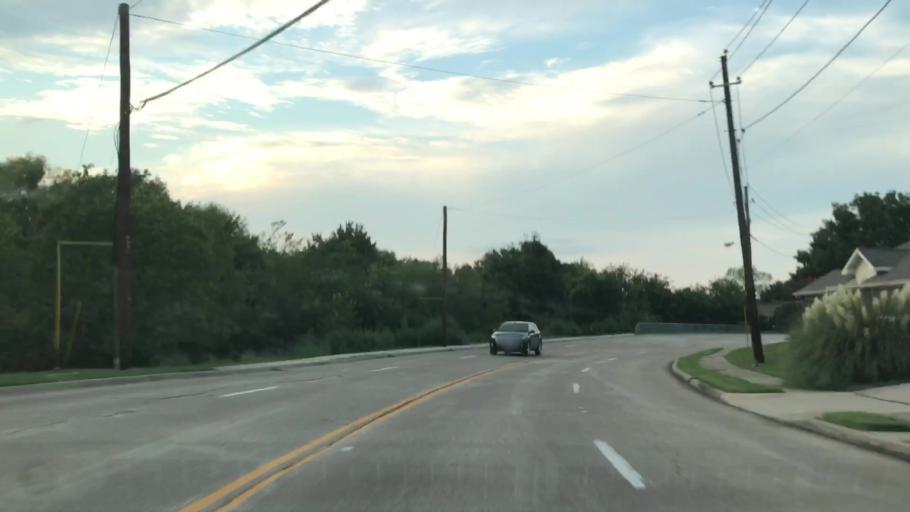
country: US
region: Texas
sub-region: Dallas County
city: Carrollton
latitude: 33.0020
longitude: -96.8657
